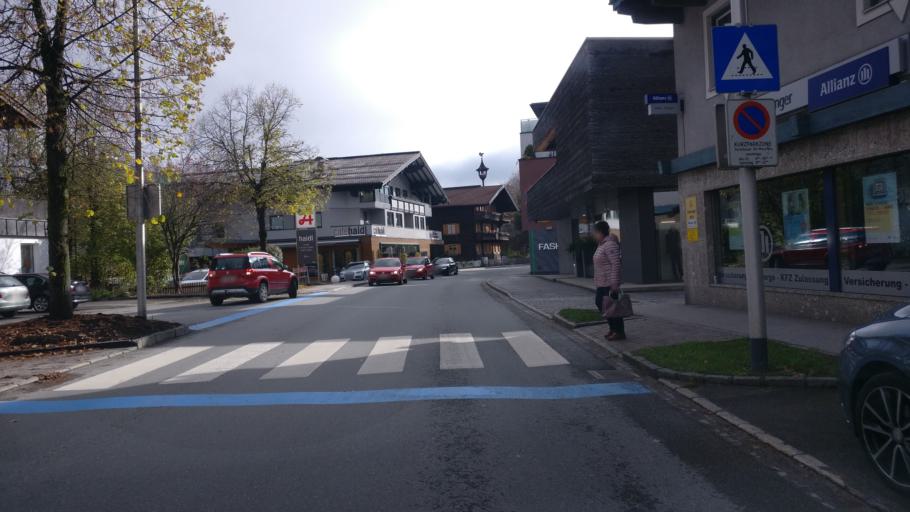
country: AT
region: Salzburg
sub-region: Politischer Bezirk Sankt Johann im Pongau
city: Altenmarkt im Pongau
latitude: 47.3811
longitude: 13.4175
